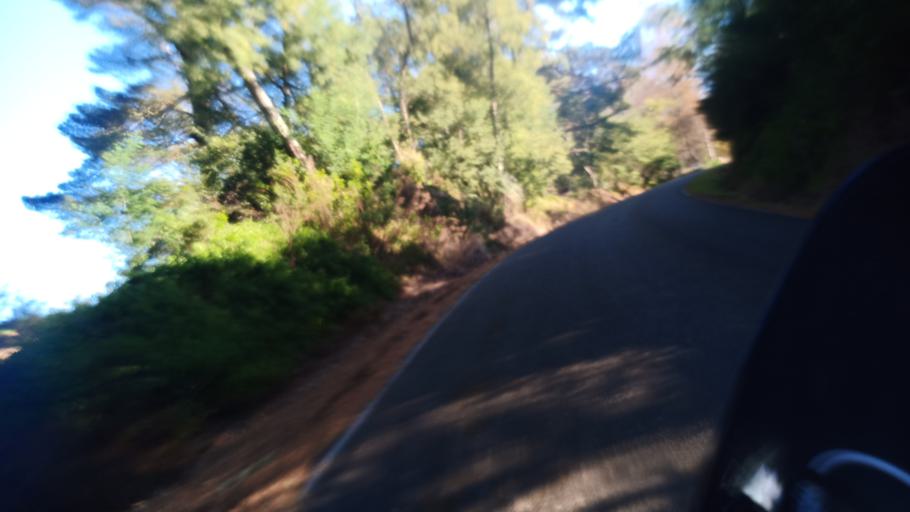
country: NZ
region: Hawke's Bay
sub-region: Wairoa District
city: Wairoa
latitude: -38.8773
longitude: 177.2351
